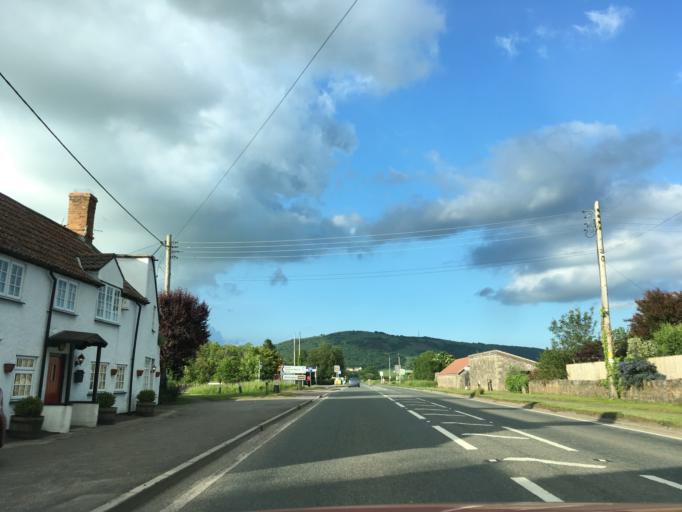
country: GB
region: England
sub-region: Somerset
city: Axbridge
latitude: 51.2803
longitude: -2.8501
